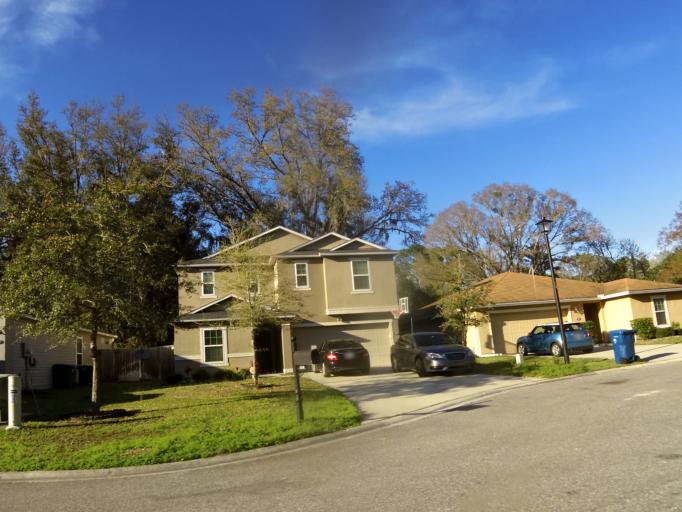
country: US
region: Florida
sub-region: Duval County
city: Jacksonville
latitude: 30.4631
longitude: -81.6229
